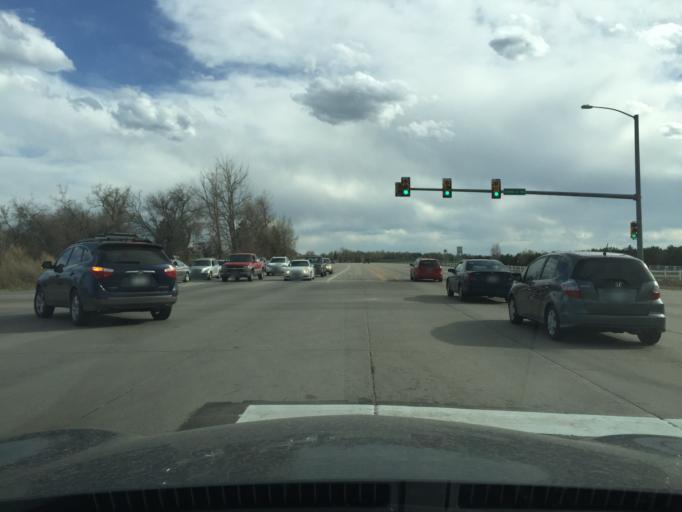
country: US
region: Colorado
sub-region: Boulder County
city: Lafayette
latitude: 40.0368
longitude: -105.1030
